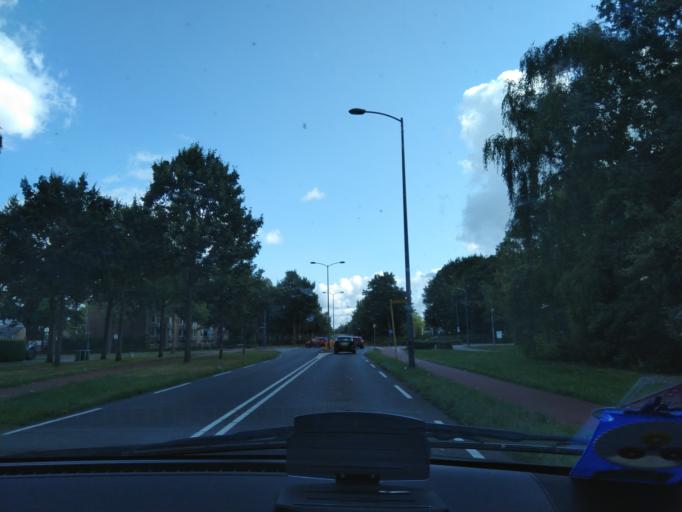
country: NL
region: North Brabant
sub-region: Gemeente Oosterhout
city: Oosterhout
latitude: 51.6233
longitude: 4.8637
